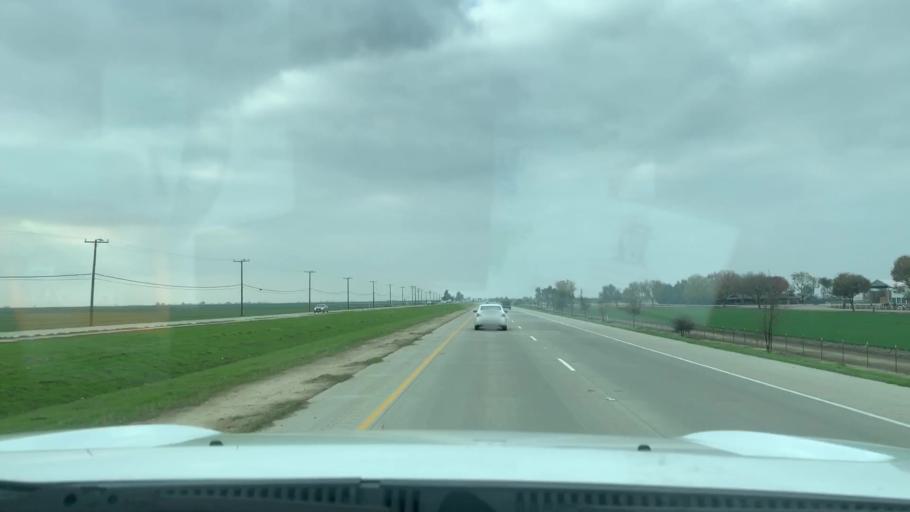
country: US
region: California
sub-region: Tulare County
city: Goshen
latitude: 36.3286
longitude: -119.5232
